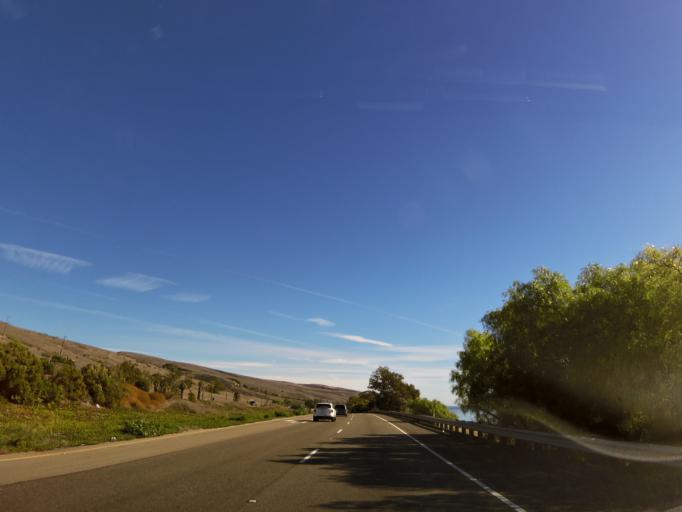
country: US
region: California
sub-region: Santa Barbara County
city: Solvang
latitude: 34.4732
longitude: -120.1311
